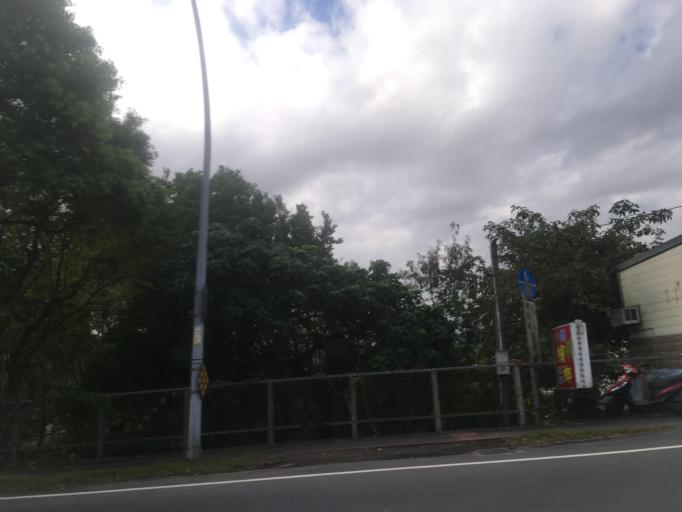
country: TW
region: Taiwan
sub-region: Yilan
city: Yilan
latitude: 24.6881
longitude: 121.7379
